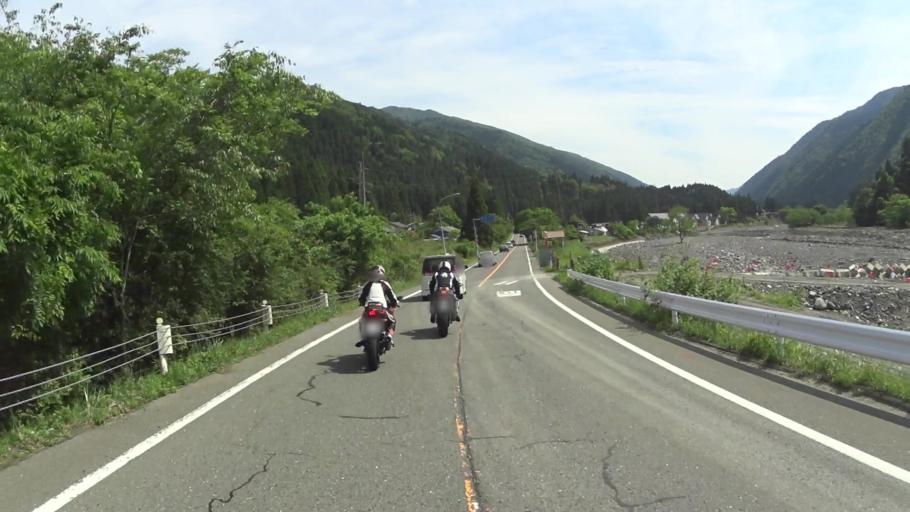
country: JP
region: Shiga Prefecture
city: Kitahama
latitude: 35.2986
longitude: 135.8868
